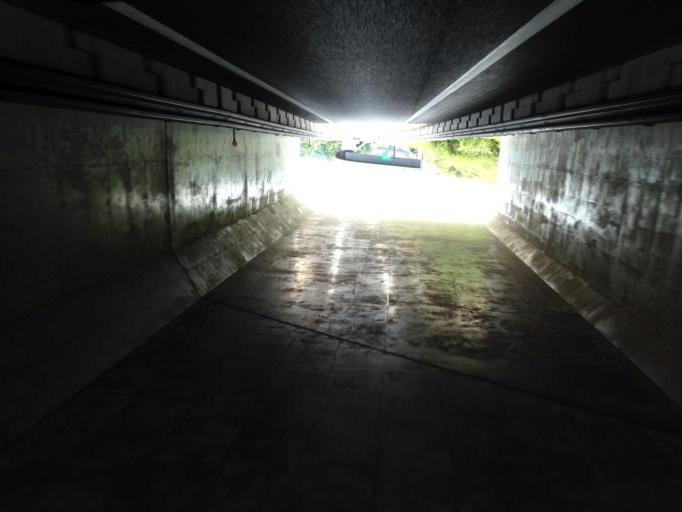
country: JP
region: Shizuoka
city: Mishima
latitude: 35.1310
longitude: 138.9431
